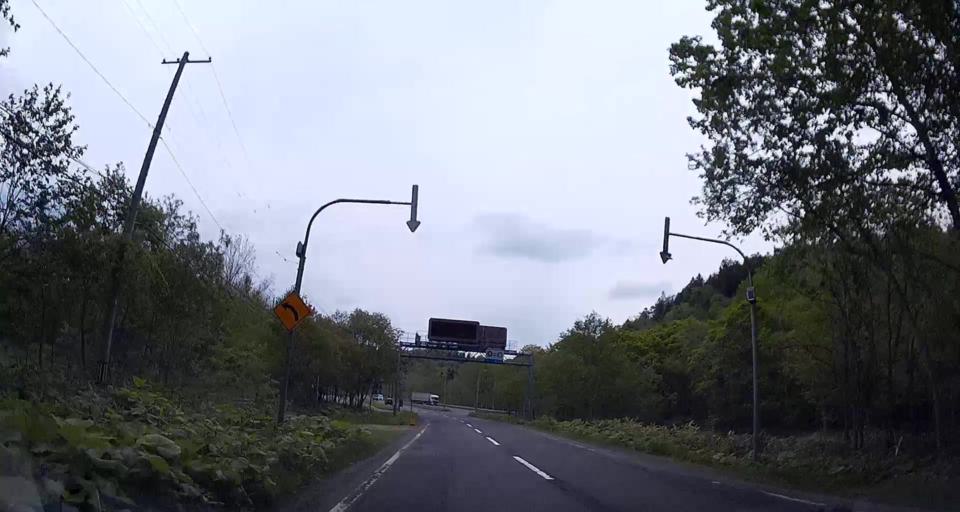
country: JP
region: Hokkaido
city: Shiraoi
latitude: 42.6925
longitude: 141.1059
